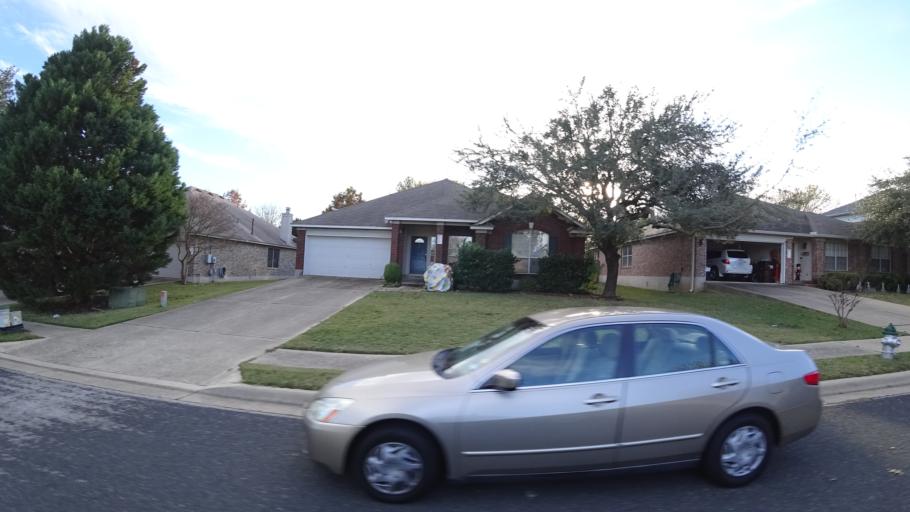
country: US
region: Texas
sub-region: Williamson County
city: Brushy Creek
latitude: 30.5029
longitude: -97.7353
